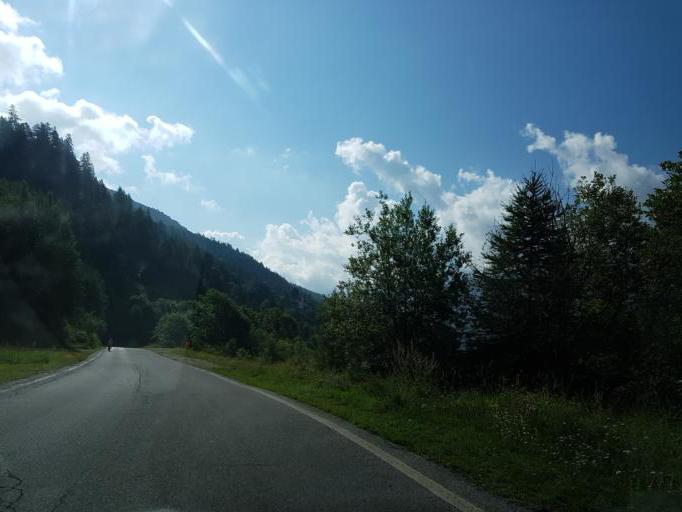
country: IT
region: Piedmont
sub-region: Provincia di Cuneo
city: Casteldelfino
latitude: 44.6098
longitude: 7.0578
